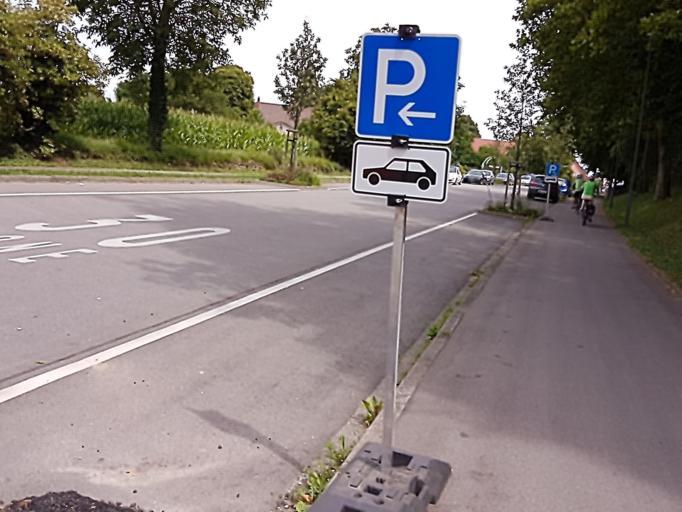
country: DE
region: Baden-Wuerttemberg
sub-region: Freiburg Region
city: Bad Krozingen
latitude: 47.9133
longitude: 7.6964
